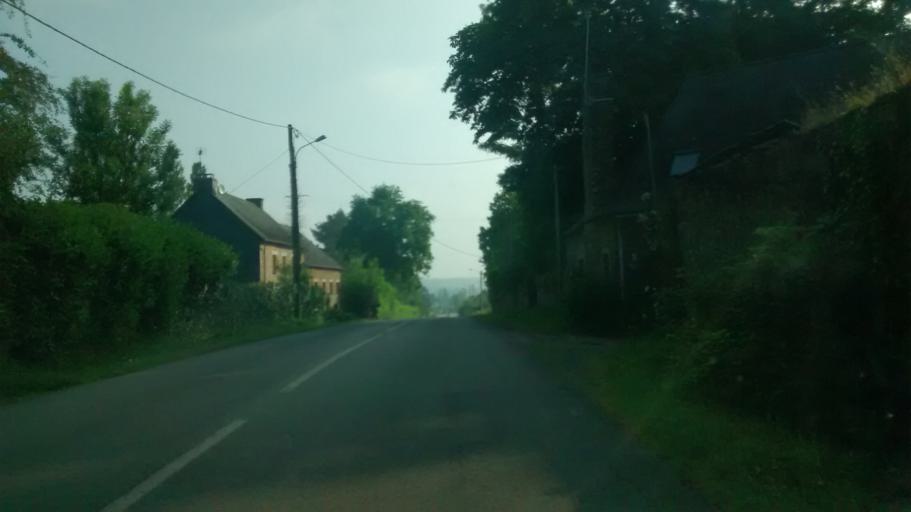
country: FR
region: Brittany
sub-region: Departement du Morbihan
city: Ruffiac
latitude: 47.8573
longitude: -2.2408
